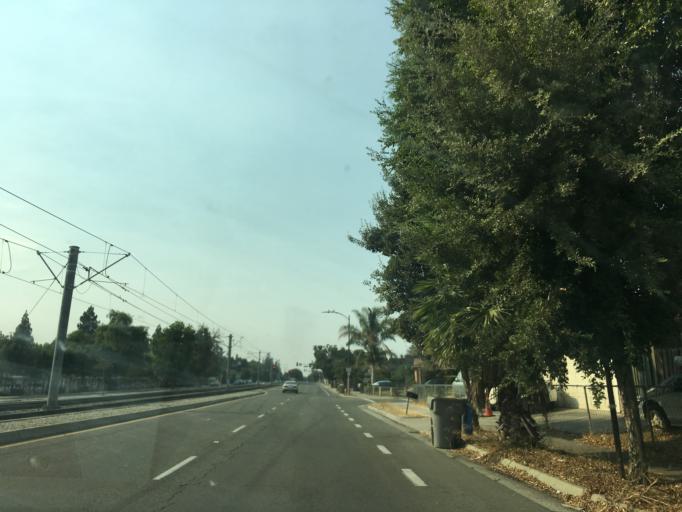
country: US
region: California
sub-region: Santa Clara County
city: Alum Rock
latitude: 37.3643
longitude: -121.8371
